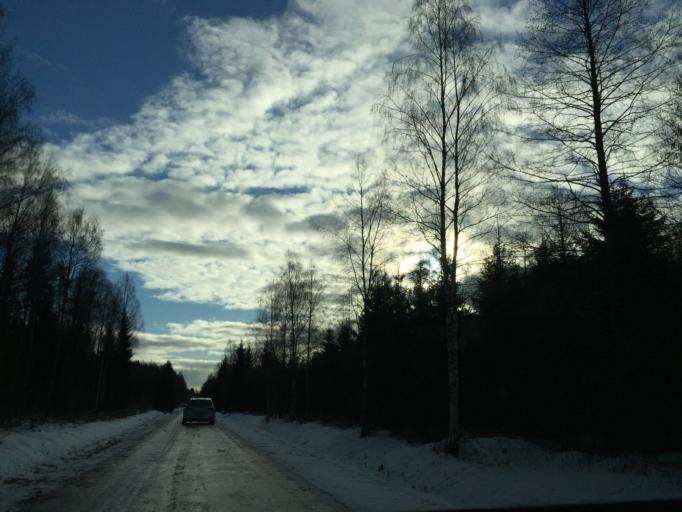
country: LV
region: Ogre
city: Jumprava
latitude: 56.5563
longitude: 24.8562
